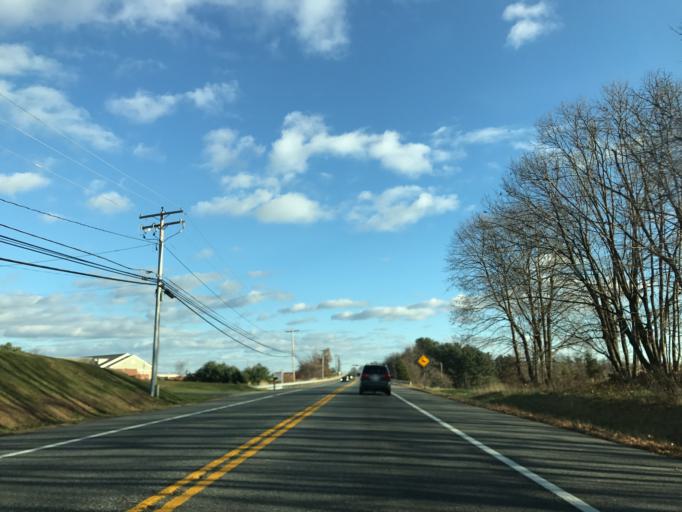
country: US
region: Maryland
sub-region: Harford County
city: Fallston
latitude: 39.5310
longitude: -76.4436
